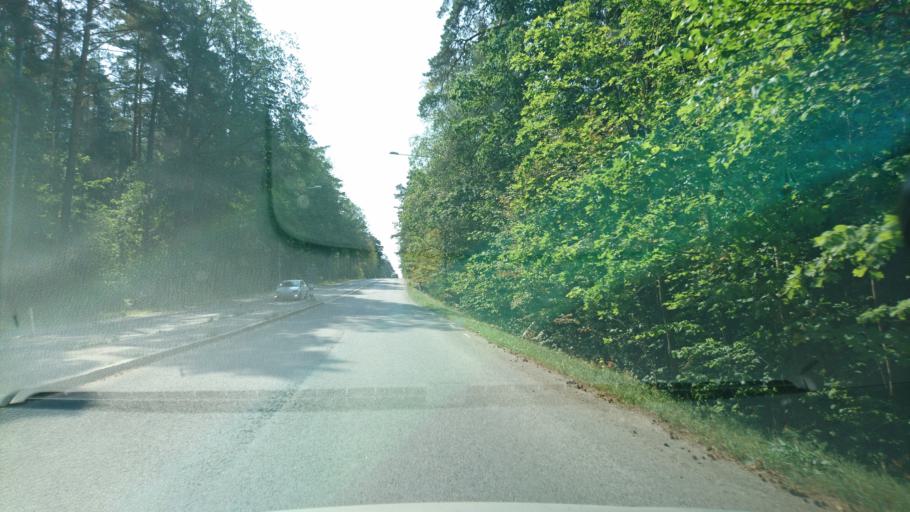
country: SE
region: Uppsala
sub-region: Uppsala Kommun
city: Uppsala
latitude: 59.8319
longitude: 17.6427
